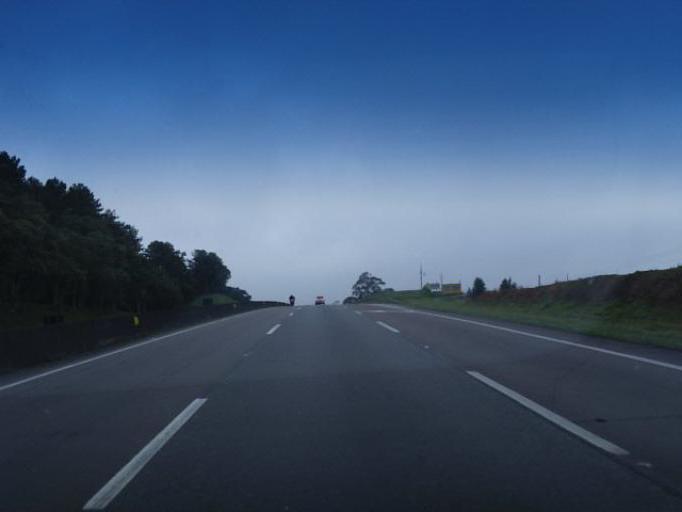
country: BR
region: Parana
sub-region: Sao Jose Dos Pinhais
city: Sao Jose dos Pinhais
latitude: -25.8136
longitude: -49.1319
